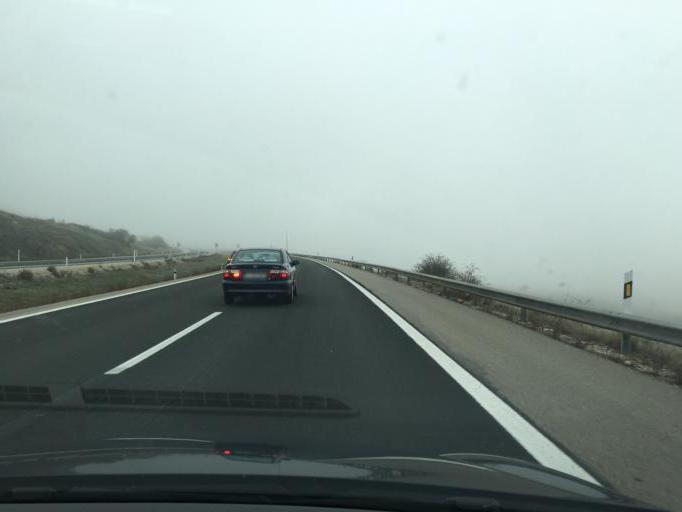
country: ES
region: Castille and Leon
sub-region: Provincia de Burgos
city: Pancorbo
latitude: 42.6237
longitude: -3.1356
